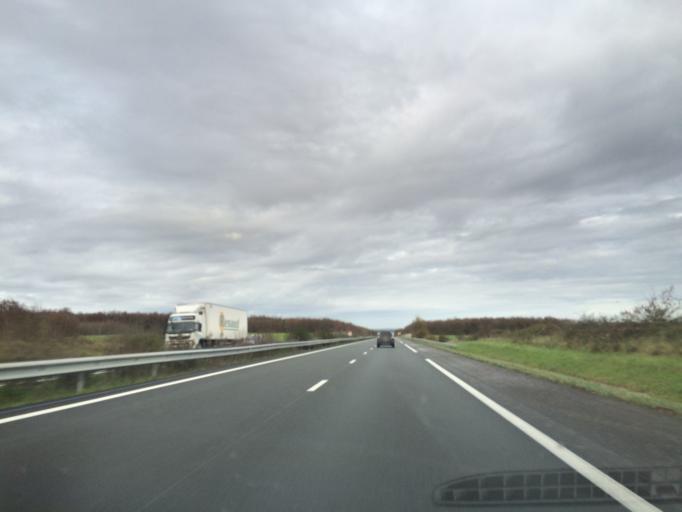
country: FR
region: Poitou-Charentes
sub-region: Departement des Deux-Sevres
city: Beauvoir-sur-Niort
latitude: 46.1868
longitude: -0.4935
